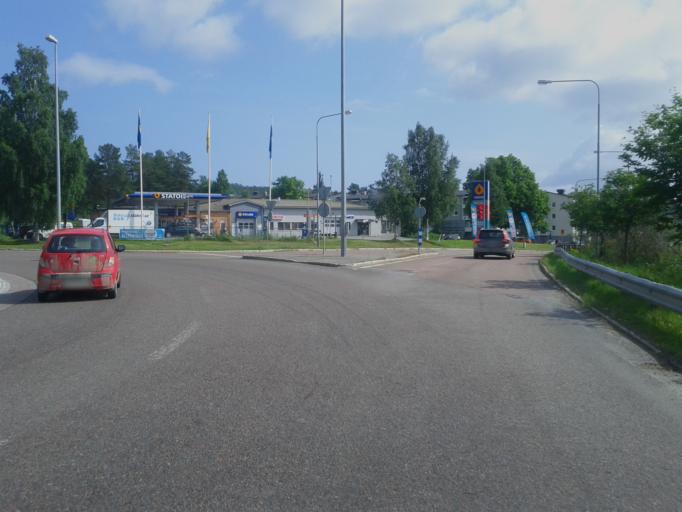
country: SE
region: Vaesterbotten
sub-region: Skelleftea Kommun
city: Skelleftea
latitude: 64.7577
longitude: 20.9648
